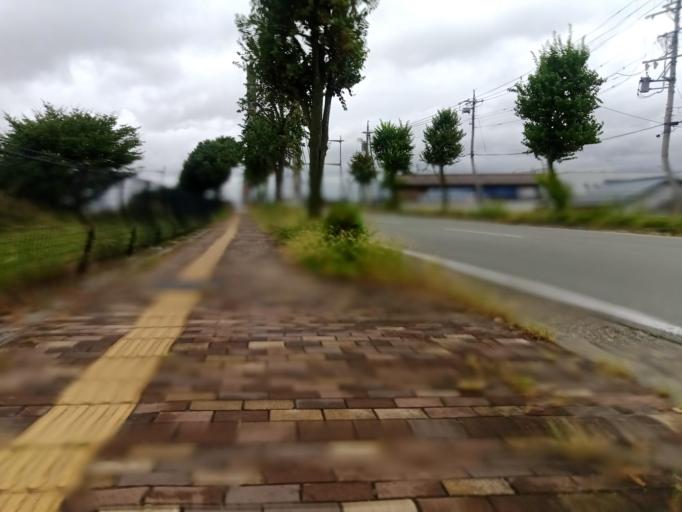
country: JP
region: Nagano
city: Nagano-shi
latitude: 36.6290
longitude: 138.1782
